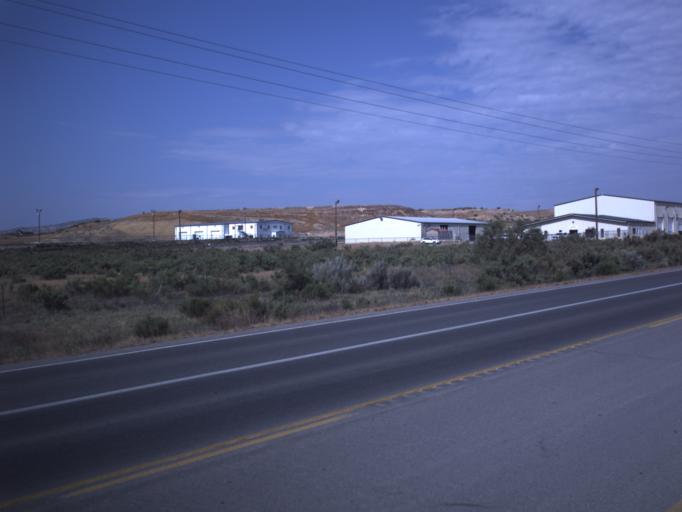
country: US
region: Utah
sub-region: Uintah County
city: Naples
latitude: 40.3888
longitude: -109.4397
